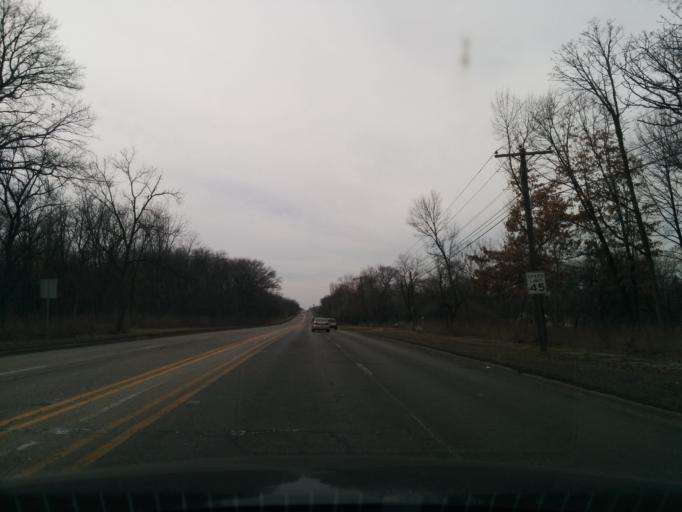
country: US
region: Illinois
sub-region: Cook County
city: Western Springs
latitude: 41.8336
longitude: -87.9034
